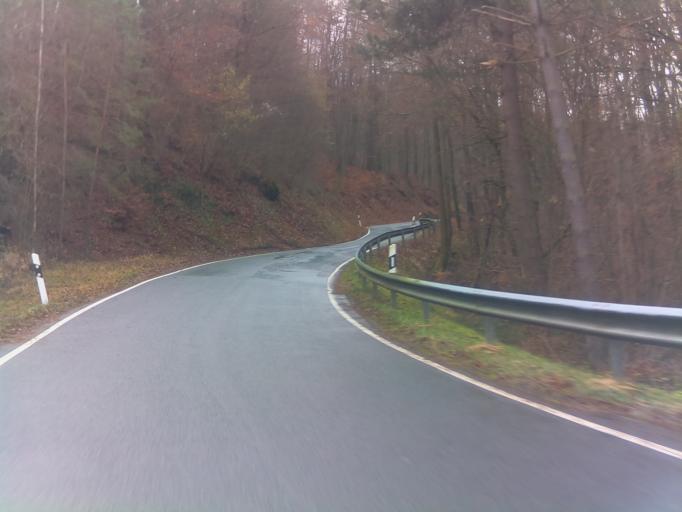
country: DE
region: Rheinland-Pfalz
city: Rockenhausen
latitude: 49.6194
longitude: 7.8456
